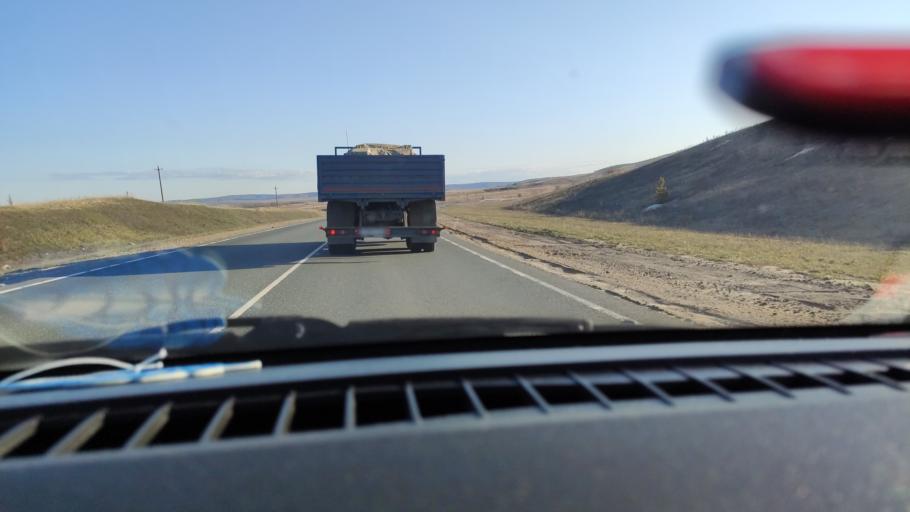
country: RU
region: Saratov
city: Alekseyevka
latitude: 52.3300
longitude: 47.9213
